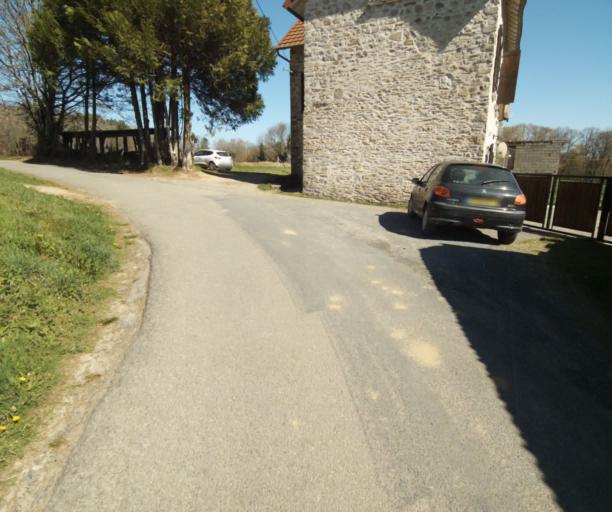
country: FR
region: Limousin
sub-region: Departement de la Correze
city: Chameyrat
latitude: 45.2449
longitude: 1.7007
